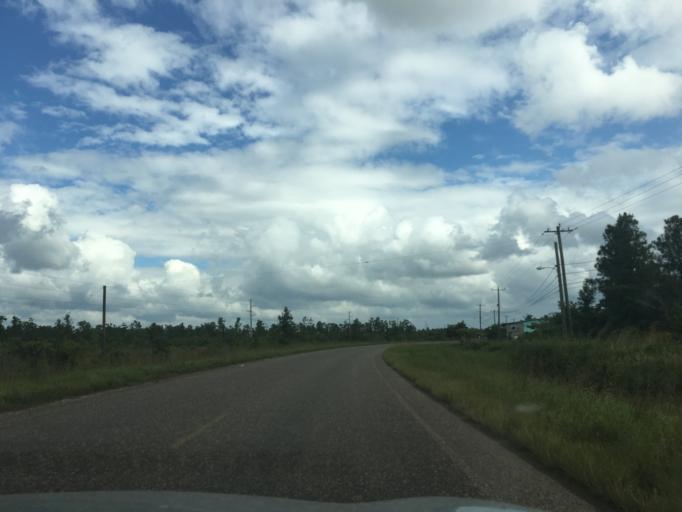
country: BZ
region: Stann Creek
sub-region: Dangriga
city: Dangriga
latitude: 16.8696
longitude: -88.3481
